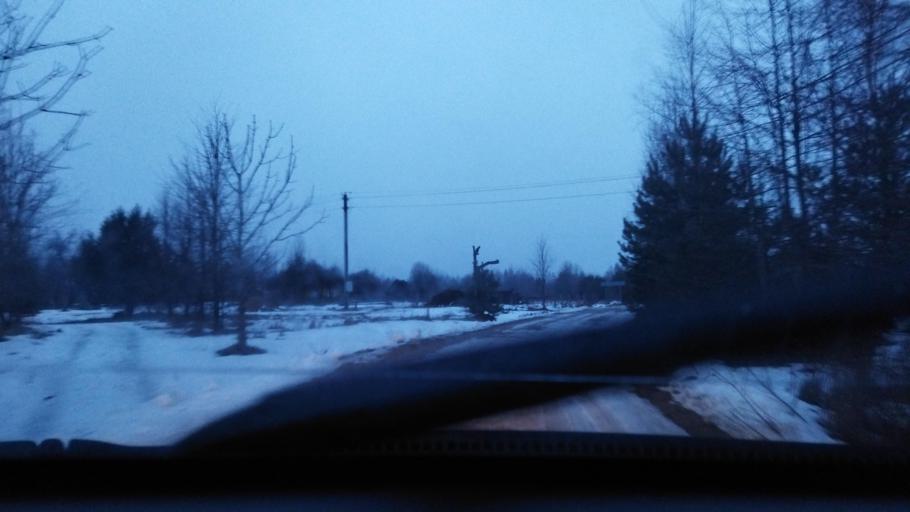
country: BY
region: Minsk
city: Svir
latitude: 54.9385
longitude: 26.3990
